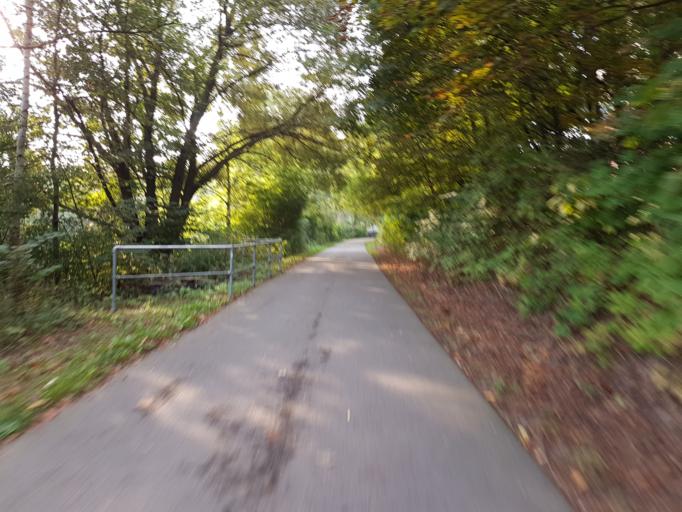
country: DE
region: Saxony
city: Chemnitz
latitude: 50.8590
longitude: 12.9236
